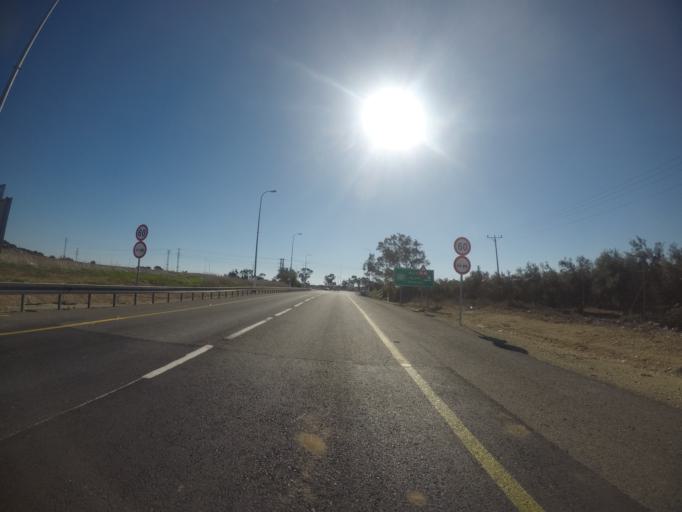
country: IL
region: Southern District
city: Ashqelon
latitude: 31.6845
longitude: 34.6525
